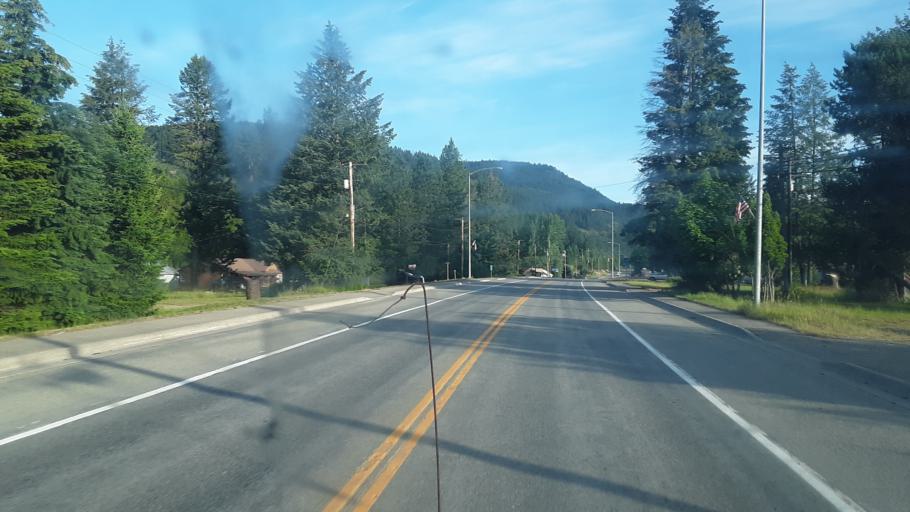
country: US
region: Montana
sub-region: Lincoln County
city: Libby
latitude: 48.4514
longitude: -115.8839
